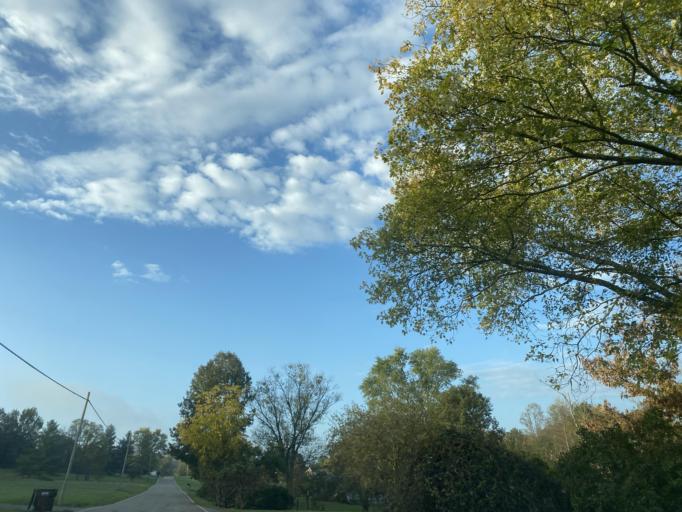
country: US
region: Kentucky
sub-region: Pendleton County
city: Falmouth
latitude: 38.7784
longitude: -84.3338
